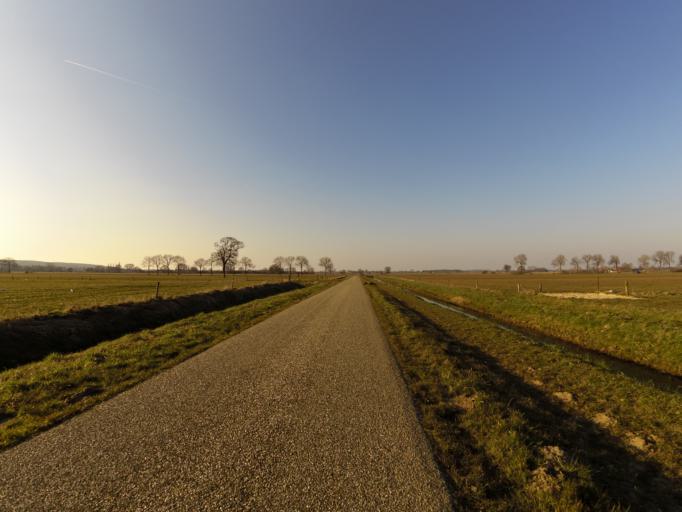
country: NL
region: Gelderland
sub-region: Gemeente Montferland
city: s-Heerenberg
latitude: 51.9051
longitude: 6.2844
